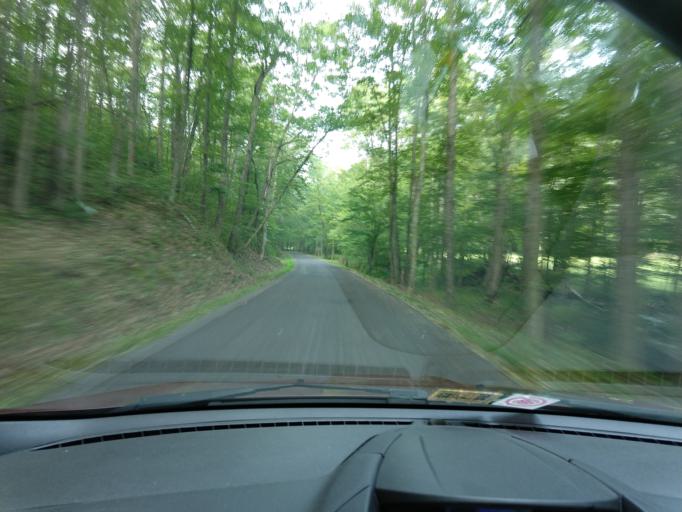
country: US
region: Virginia
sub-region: City of Covington
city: Covington
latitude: 37.9017
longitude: -80.0834
